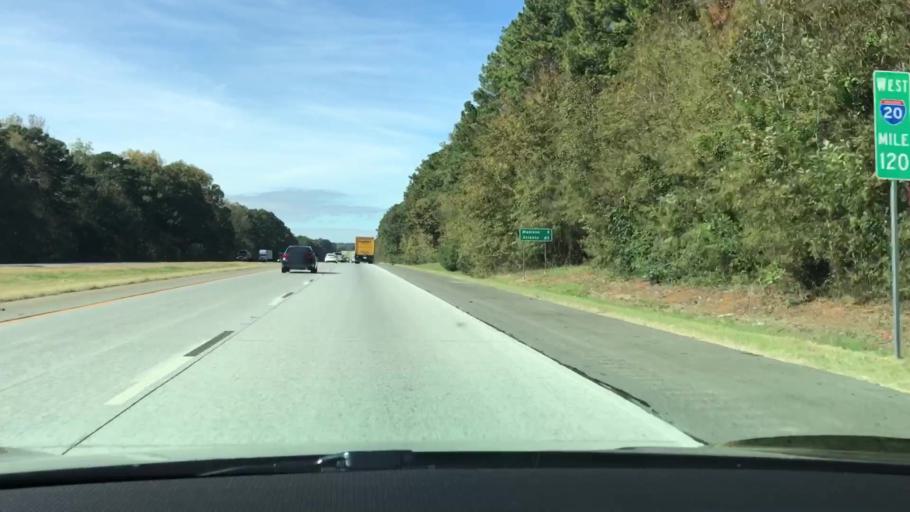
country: US
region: Georgia
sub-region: Morgan County
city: Madison
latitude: 33.5553
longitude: -83.3782
